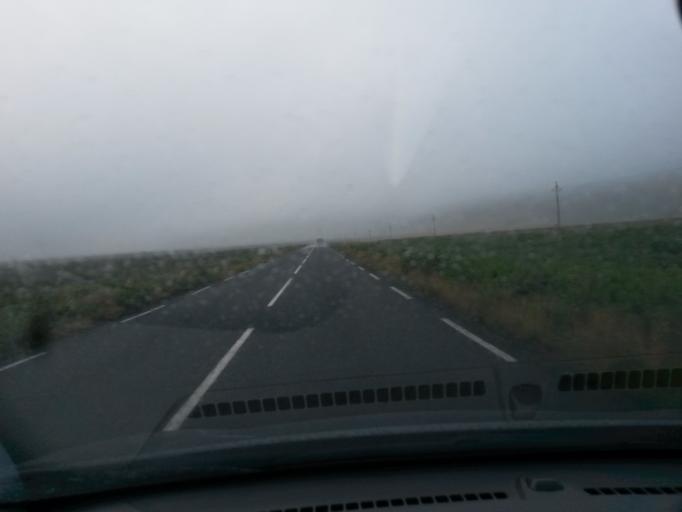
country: IS
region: South
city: Vestmannaeyjar
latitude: 63.5122
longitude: -19.4522
